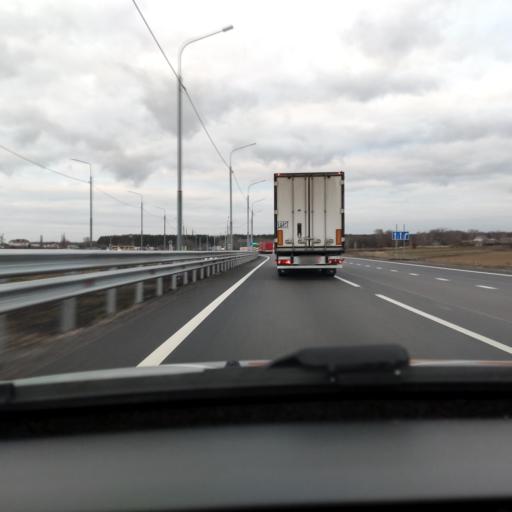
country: RU
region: Lipetsk
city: Khlevnoye
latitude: 52.0707
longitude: 39.1816
